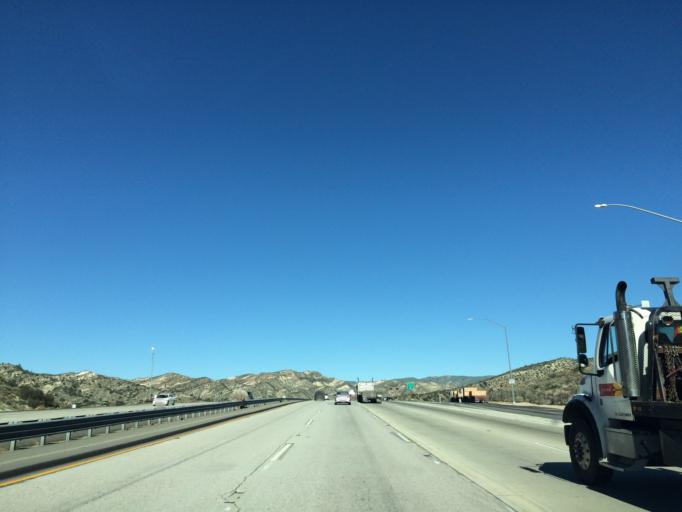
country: US
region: California
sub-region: Kern County
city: Lebec
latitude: 34.7048
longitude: -118.7947
